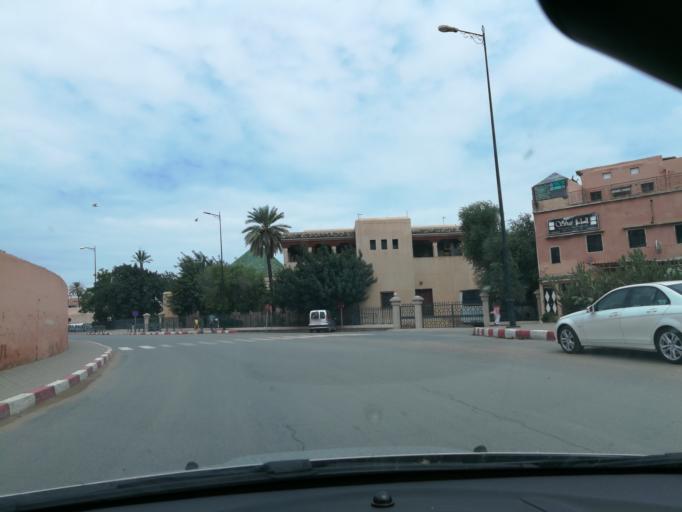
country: MA
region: Marrakech-Tensift-Al Haouz
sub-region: Marrakech
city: Marrakesh
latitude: 31.6315
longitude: -7.9985
